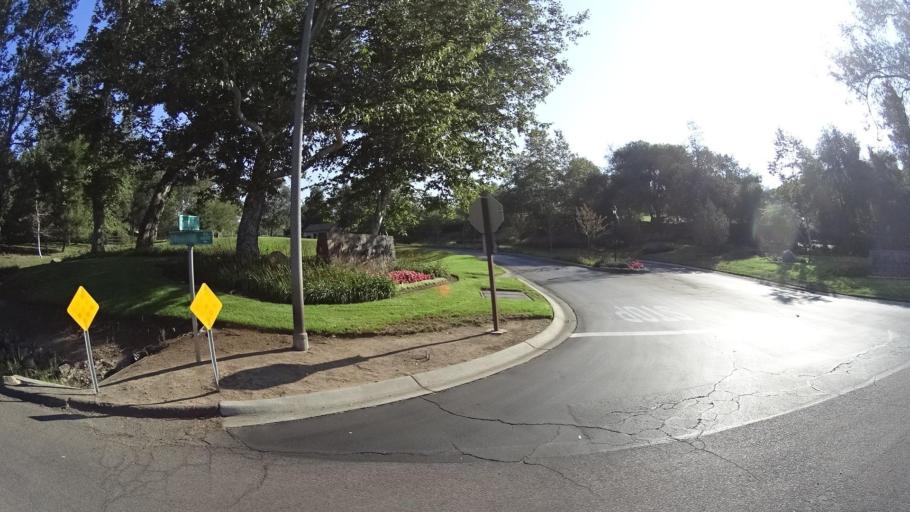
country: US
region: California
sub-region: San Diego County
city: Bonsall
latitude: 33.3032
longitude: -117.2427
